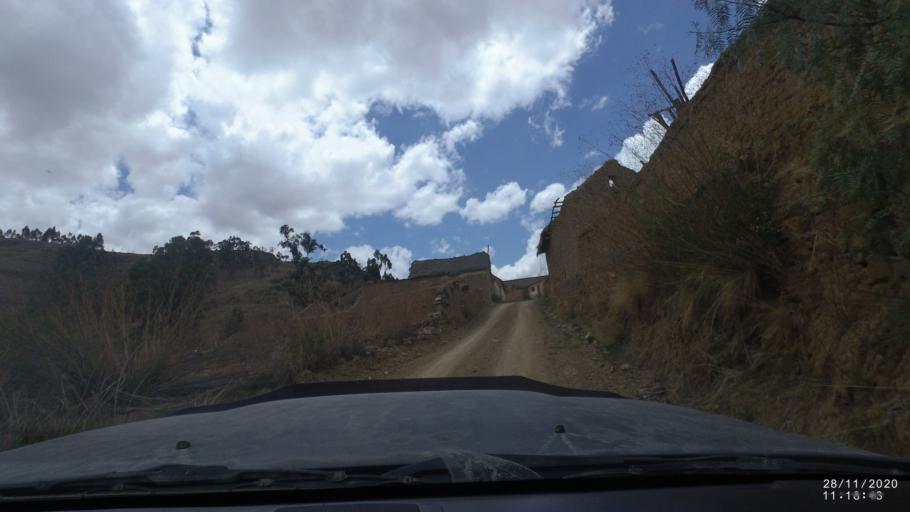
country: BO
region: Cochabamba
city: Tarata
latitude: -17.7536
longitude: -66.0725
